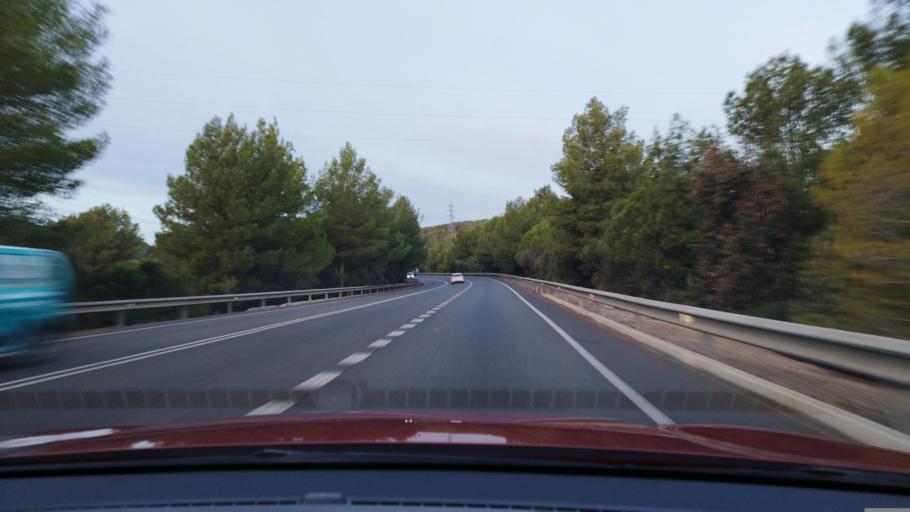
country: ES
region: Catalonia
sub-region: Provincia de Tarragona
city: Calafell
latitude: 41.2070
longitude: 1.5659
